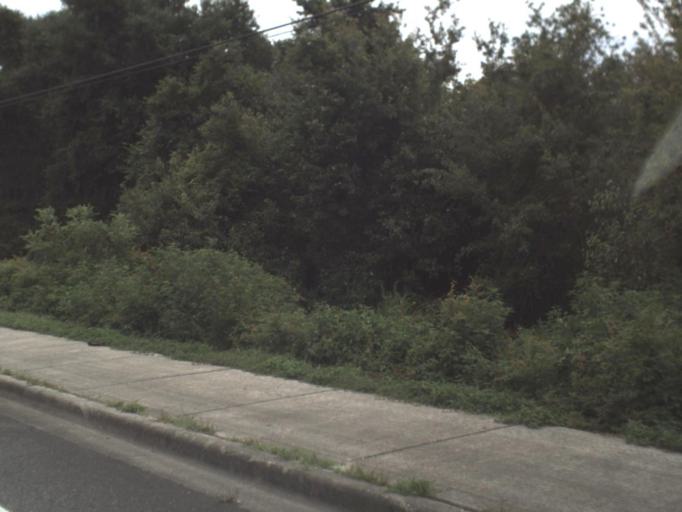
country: US
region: Florida
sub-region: Citrus County
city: Inverness
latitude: 28.8411
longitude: -82.2901
